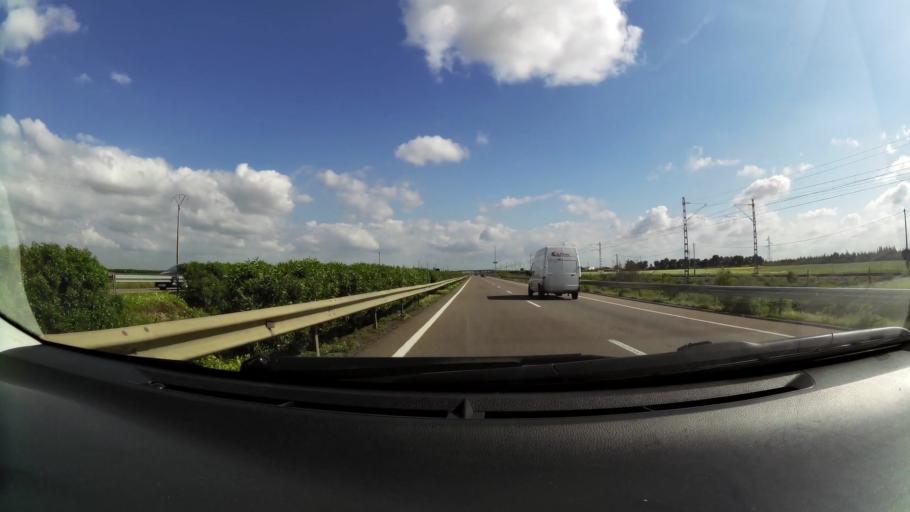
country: MA
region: Chaouia-Ouardigha
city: Nouaseur
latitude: 33.3420
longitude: -7.6126
